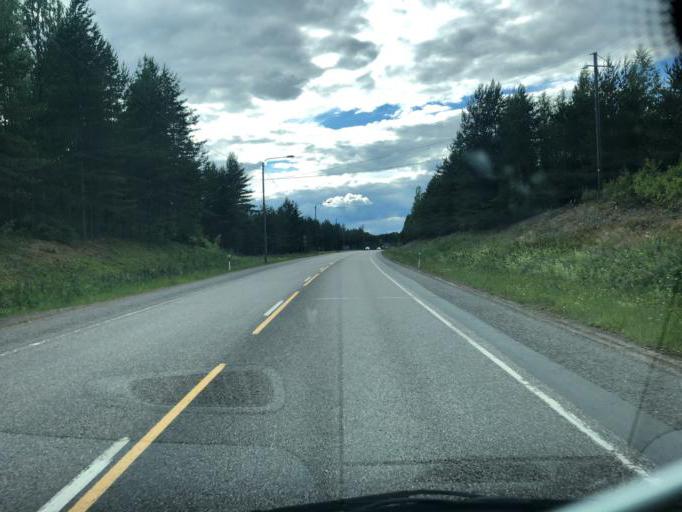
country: FI
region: Kymenlaakso
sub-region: Kouvola
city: Kouvola
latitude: 60.8661
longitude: 26.5635
